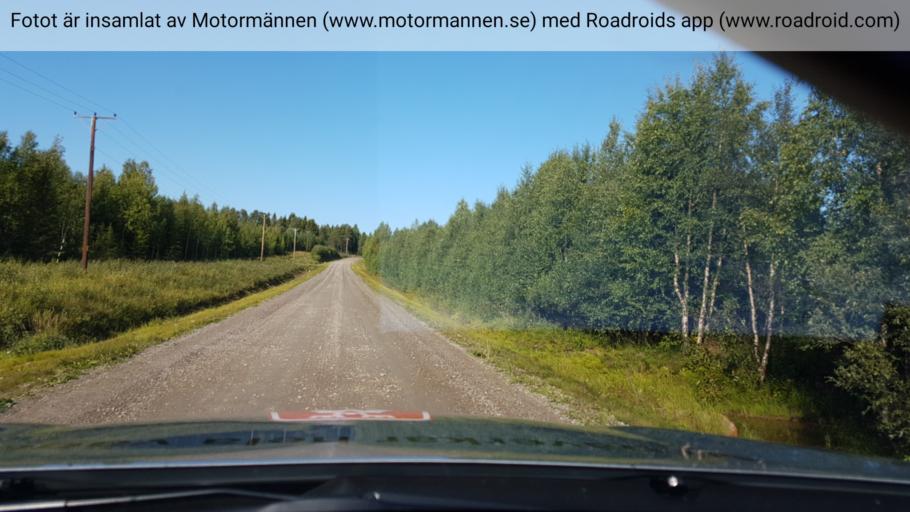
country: SE
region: Norrbotten
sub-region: Kalix Kommun
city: Kalix
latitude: 66.1349
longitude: 23.2397
